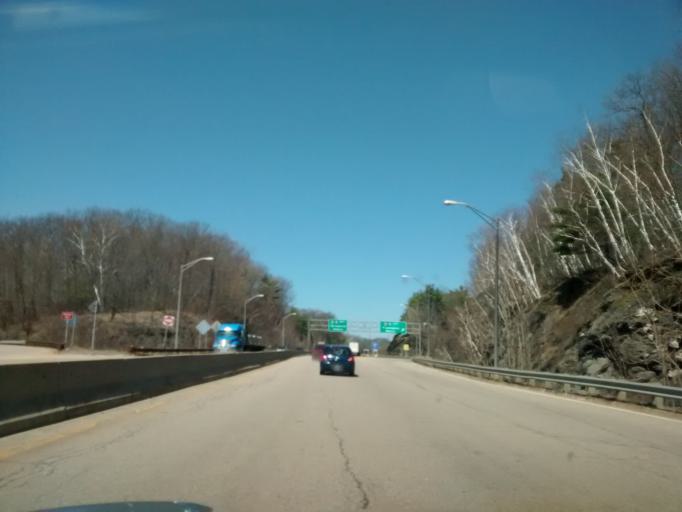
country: US
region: Massachusetts
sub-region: Worcester County
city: Auburn
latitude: 42.1896
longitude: -71.8540
